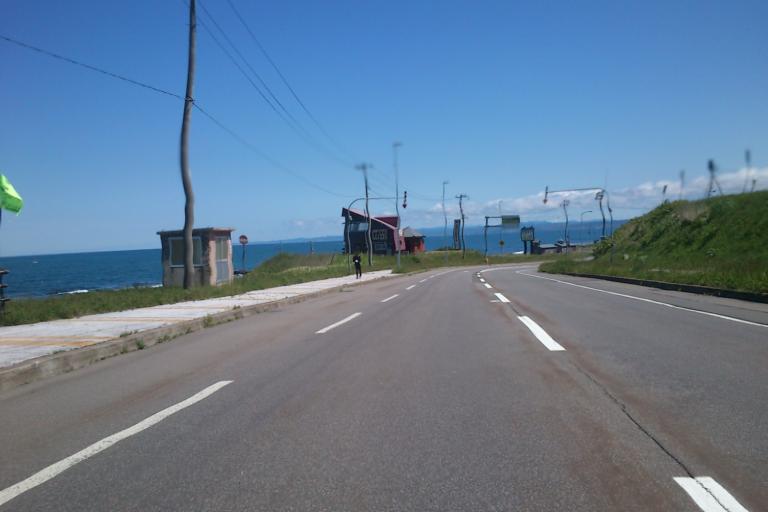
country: JP
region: Hokkaido
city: Rumoi
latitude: 43.8529
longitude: 141.5086
